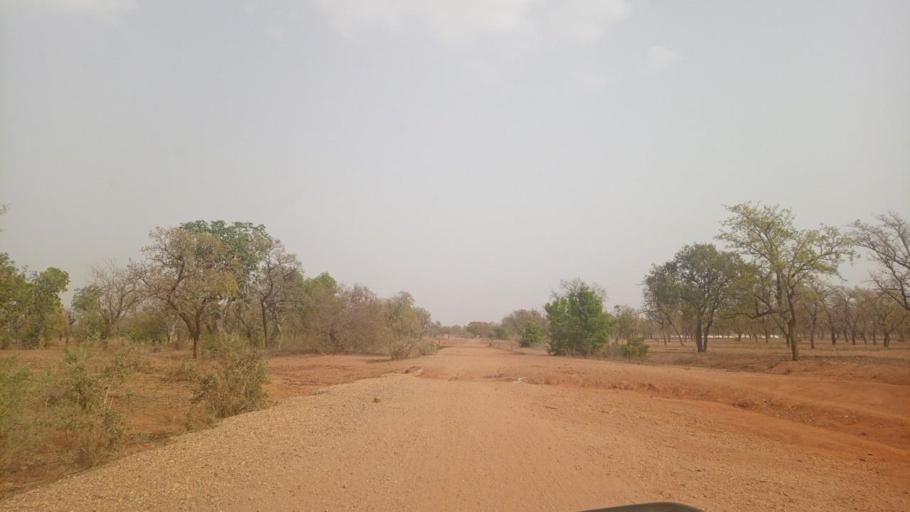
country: BF
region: Boucle du Mouhoun
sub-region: Province des Banwa
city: Salanso
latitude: 12.0961
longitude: -4.3312
